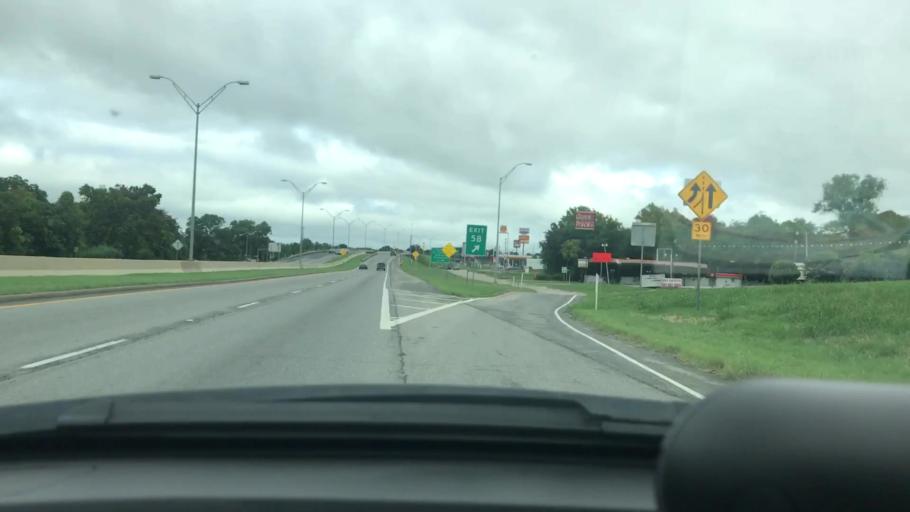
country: US
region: Texas
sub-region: Grayson County
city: Sherman
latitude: 33.6312
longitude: -96.6144
